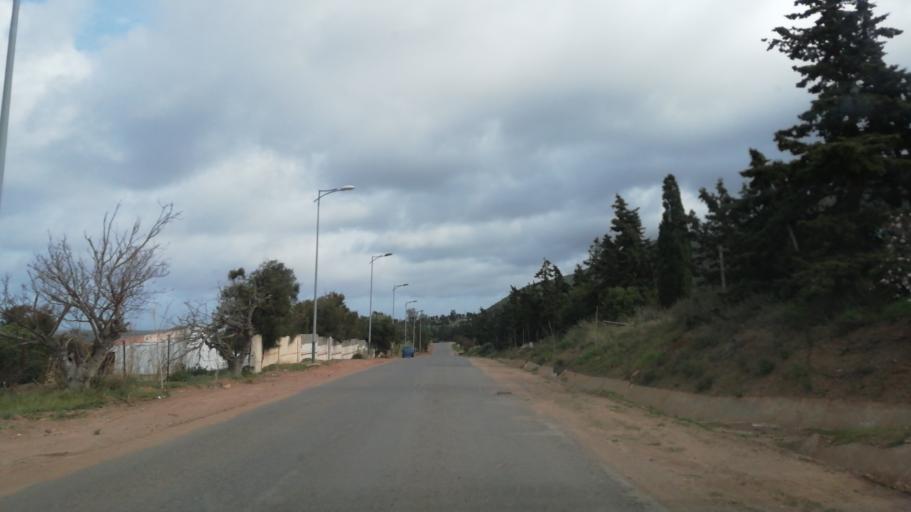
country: DZ
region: Oran
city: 'Ain el Turk
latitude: 35.6938
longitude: -0.8584
